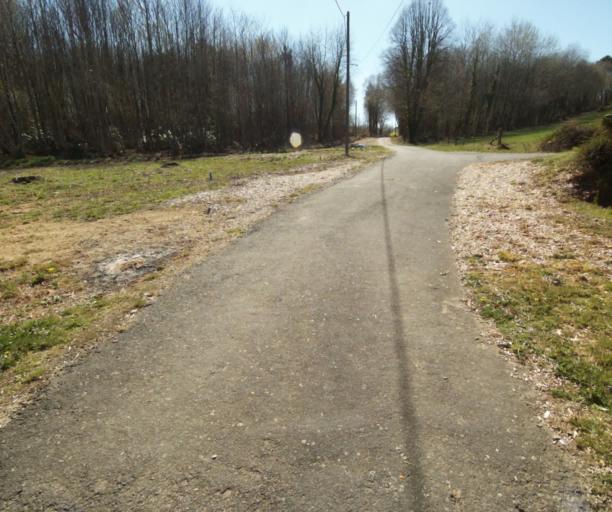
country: FR
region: Limousin
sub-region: Departement de la Correze
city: Chameyrat
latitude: 45.2711
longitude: 1.6983
